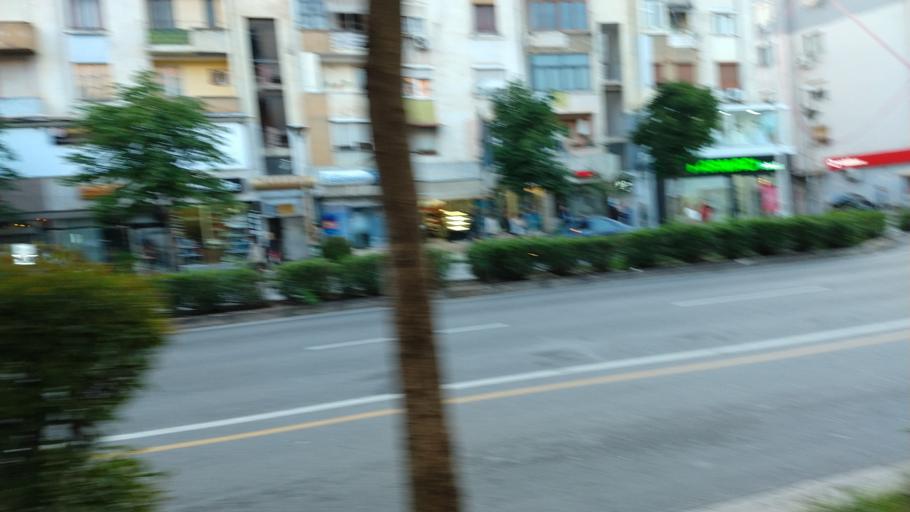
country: AL
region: Tirane
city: Tirana
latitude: 41.3252
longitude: 19.8039
